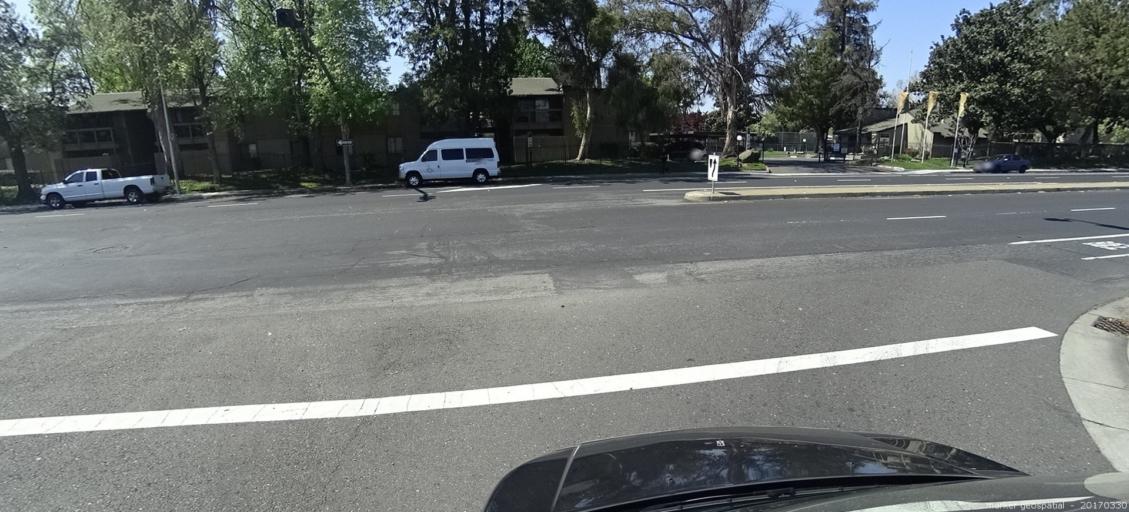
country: US
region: California
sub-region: Sacramento County
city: Florin
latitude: 38.4686
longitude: -121.4270
